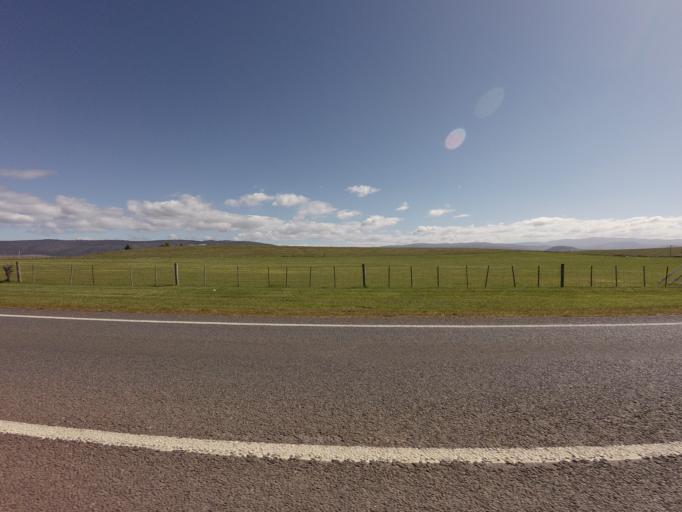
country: AU
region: Tasmania
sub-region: Derwent Valley
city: New Norfolk
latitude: -42.7036
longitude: 146.9427
